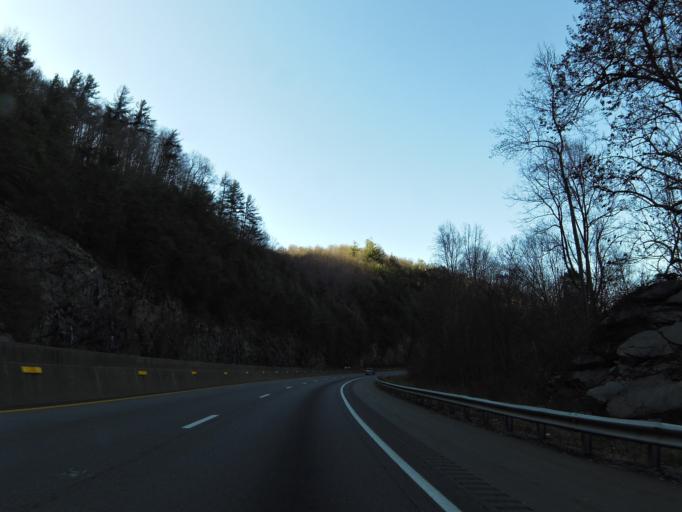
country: US
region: North Carolina
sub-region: Haywood County
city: Cove Creek
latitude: 35.7045
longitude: -83.0296
